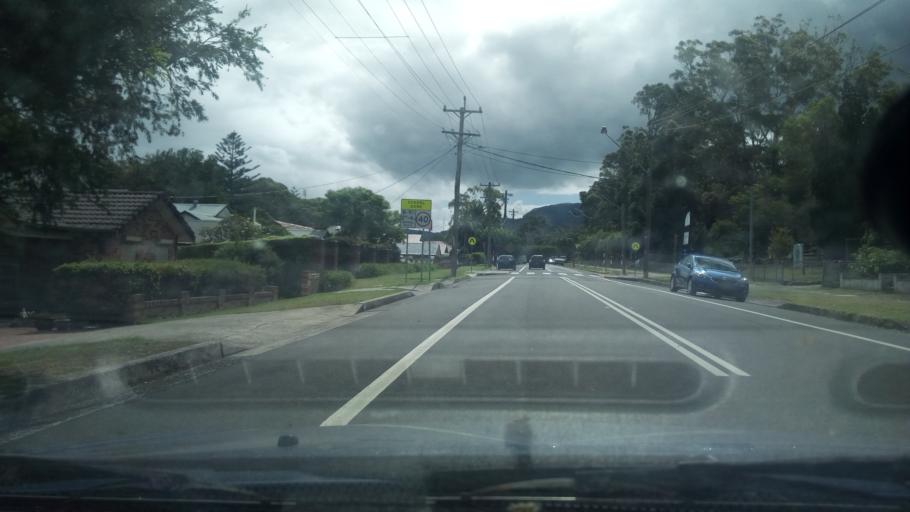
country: AU
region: New South Wales
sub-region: Wollongong
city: Gwynneville
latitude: -34.4185
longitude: 150.8802
